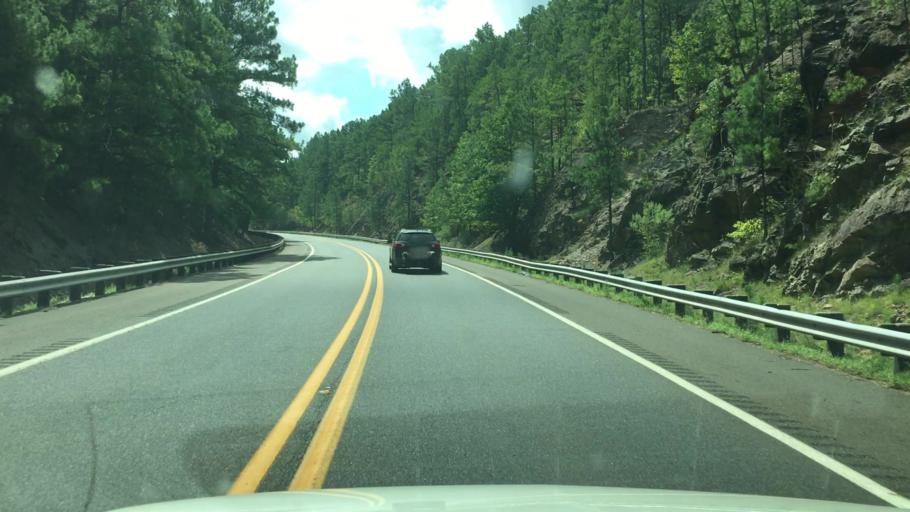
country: US
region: Arkansas
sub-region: Clark County
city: Arkadelphia
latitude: 34.2320
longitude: -93.0994
